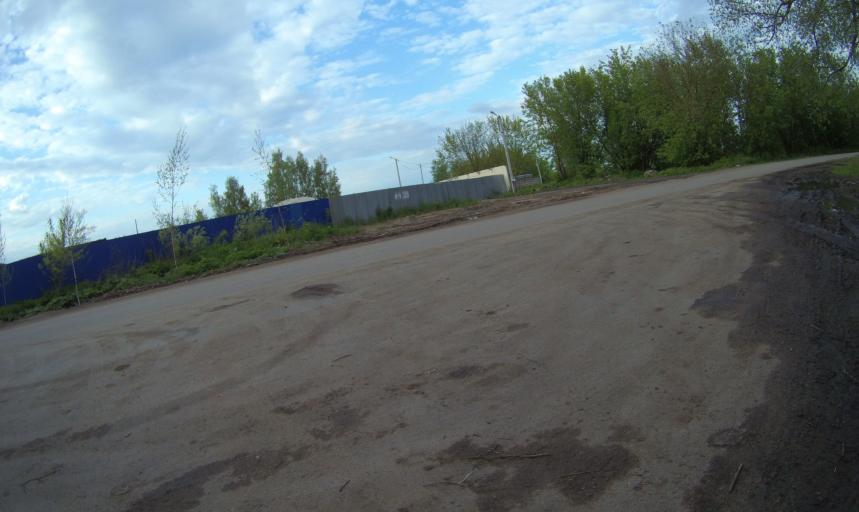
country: RU
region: Moskovskaya
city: Ramenskoye
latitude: 55.5656
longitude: 38.2750
